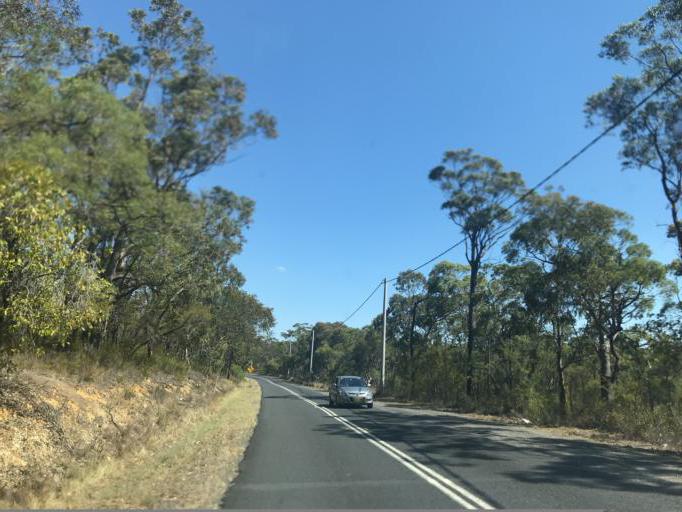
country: AU
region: New South Wales
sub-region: Hawkesbury
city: Pitt Town
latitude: -33.4581
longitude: 150.8576
